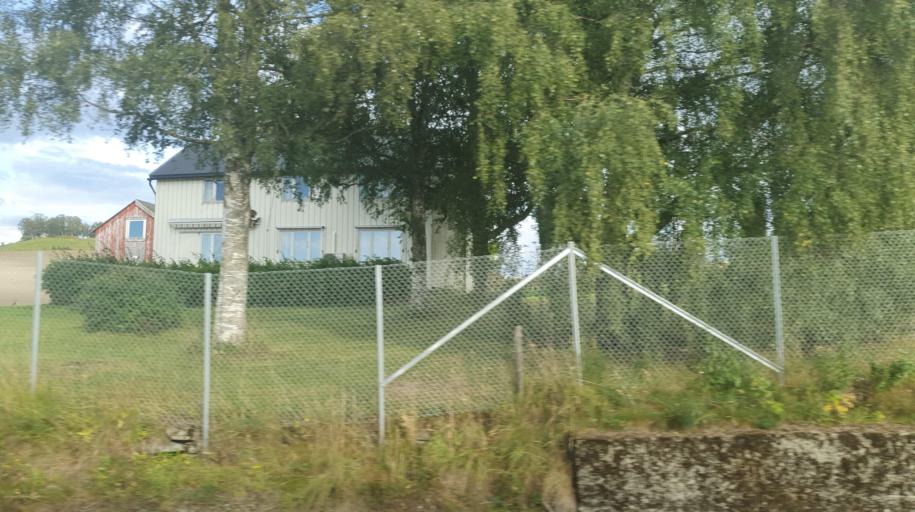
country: NO
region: Nord-Trondelag
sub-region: Levanger
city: Skogn
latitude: 63.7083
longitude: 11.1973
